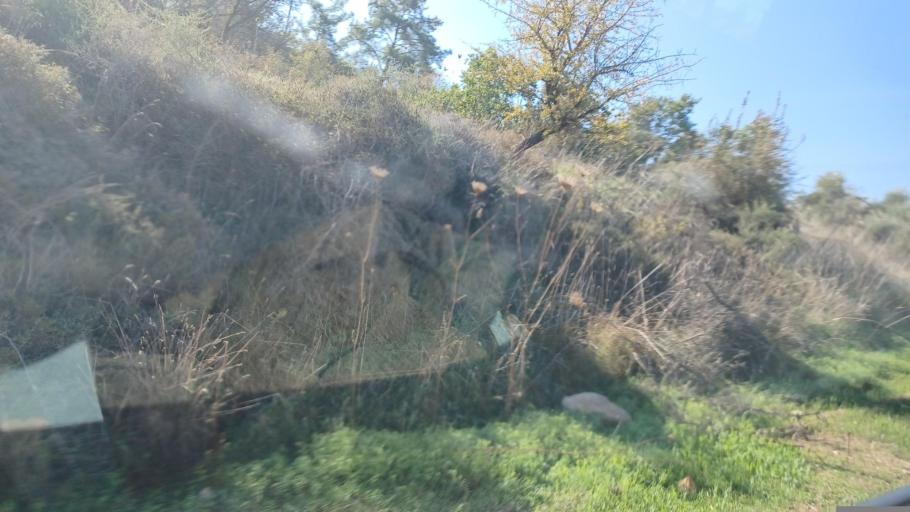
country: CY
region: Pafos
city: Polis
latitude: 35.0367
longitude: 32.5063
